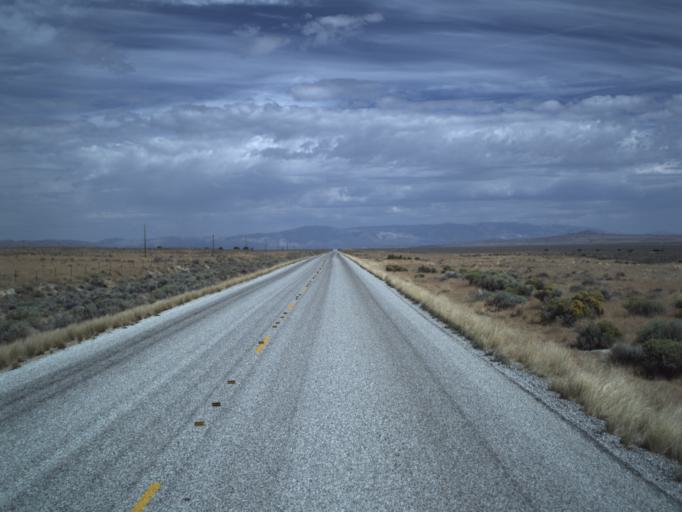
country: US
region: Utah
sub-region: Tooele County
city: Wendover
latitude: 41.5134
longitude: -113.5999
